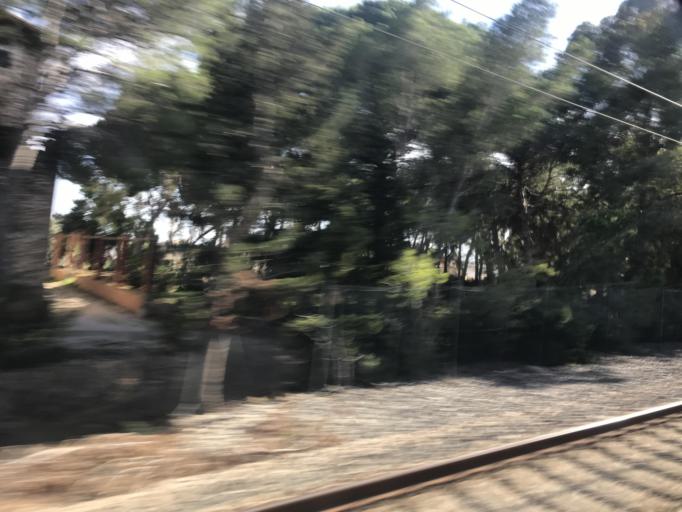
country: ES
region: Catalonia
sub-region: Provincia de Tarragona
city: L'Ampolla
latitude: 40.8067
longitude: 0.6998
